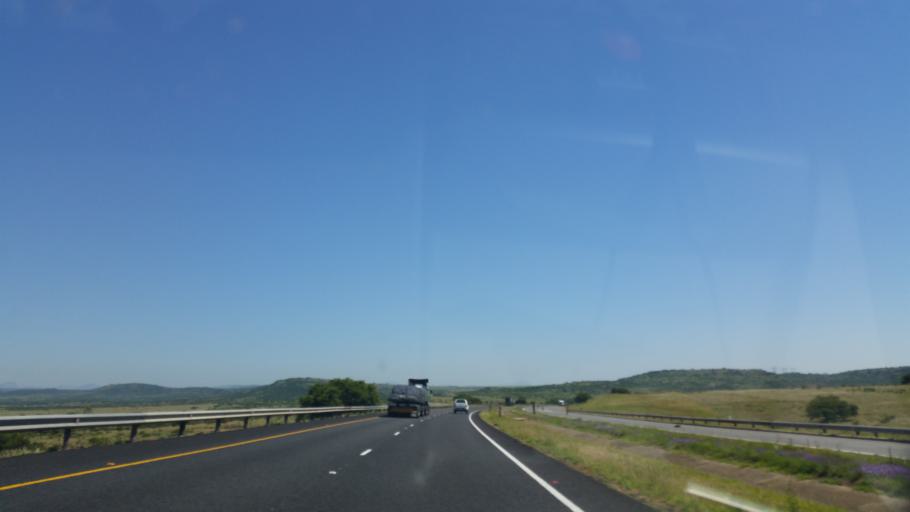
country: ZA
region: KwaZulu-Natal
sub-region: uThukela District Municipality
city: Ladysmith
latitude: -28.7063
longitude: 29.6404
